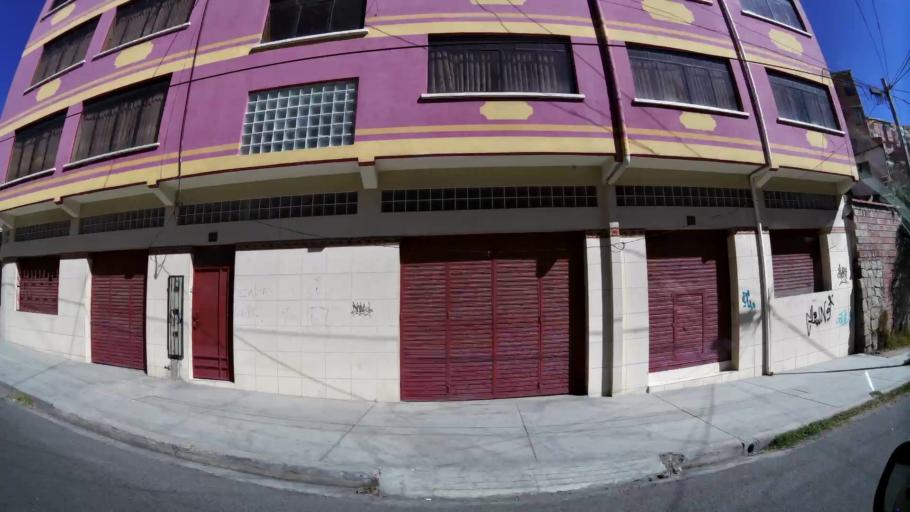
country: BO
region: La Paz
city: La Paz
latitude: -16.4880
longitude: -68.1485
